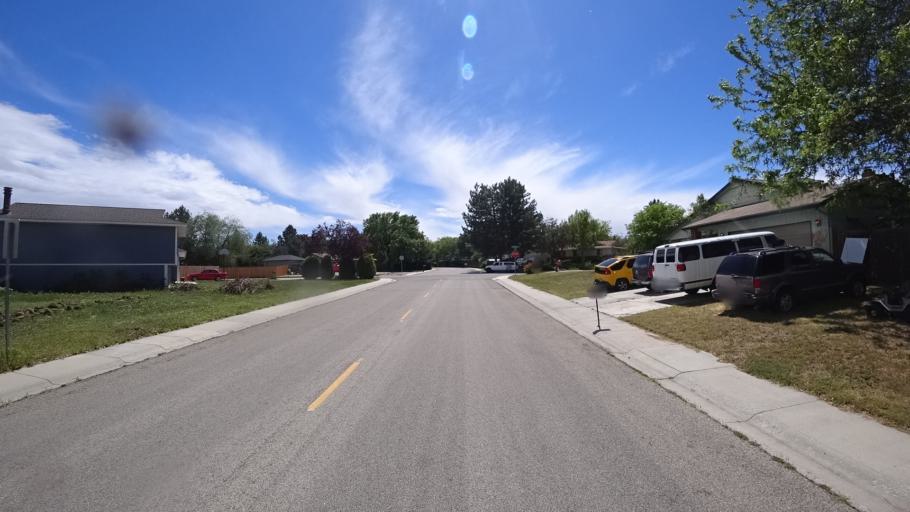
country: US
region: Idaho
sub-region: Ada County
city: Meridian
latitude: 43.5666
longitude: -116.3256
